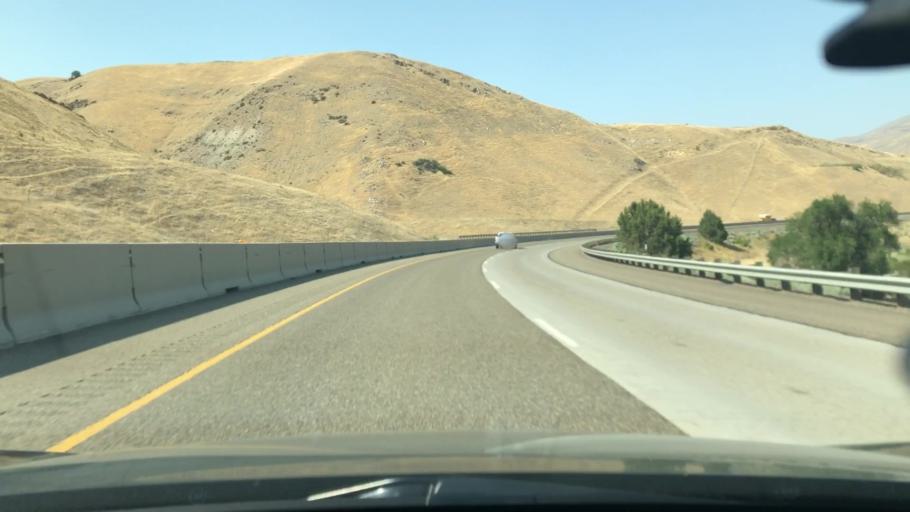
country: US
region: Idaho
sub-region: Washington County
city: Weiser
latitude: 44.4059
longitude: -117.3130
